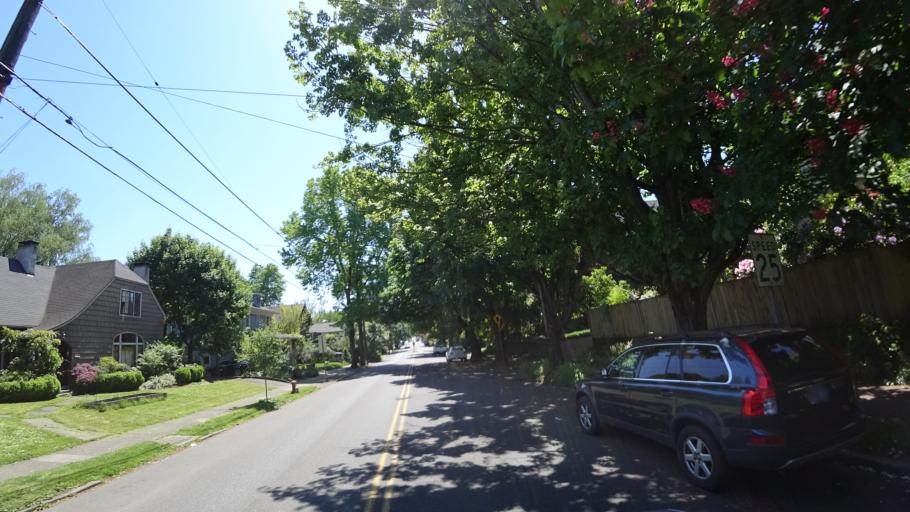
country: US
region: Oregon
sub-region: Multnomah County
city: Portland
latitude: 45.5400
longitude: -122.6505
